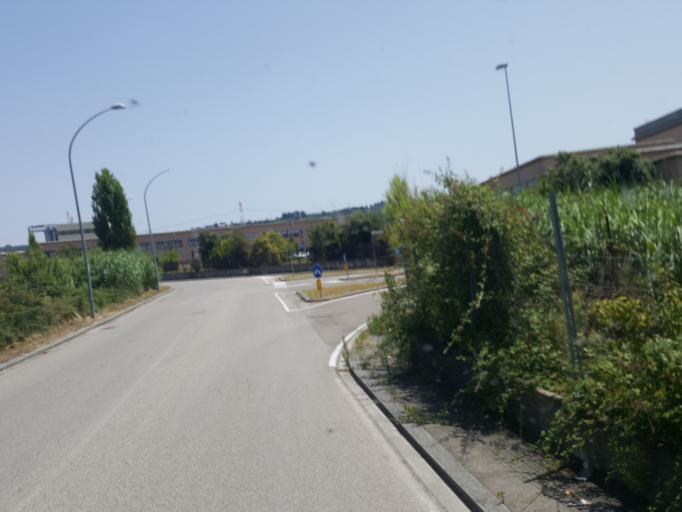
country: IT
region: Tuscany
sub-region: Province of Florence
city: Montelupo Fiorentino
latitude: 43.7253
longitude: 10.9902
